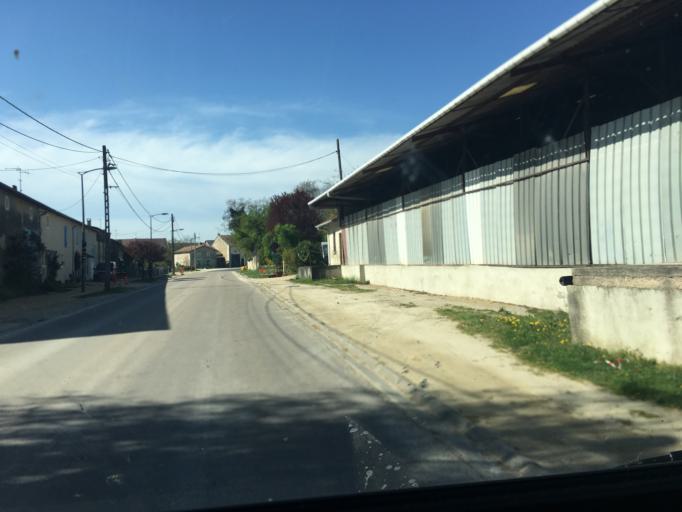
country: FR
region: Lorraine
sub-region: Departement de la Meuse
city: Vigneulles-les-Hattonchatel
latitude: 48.9339
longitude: 5.6999
